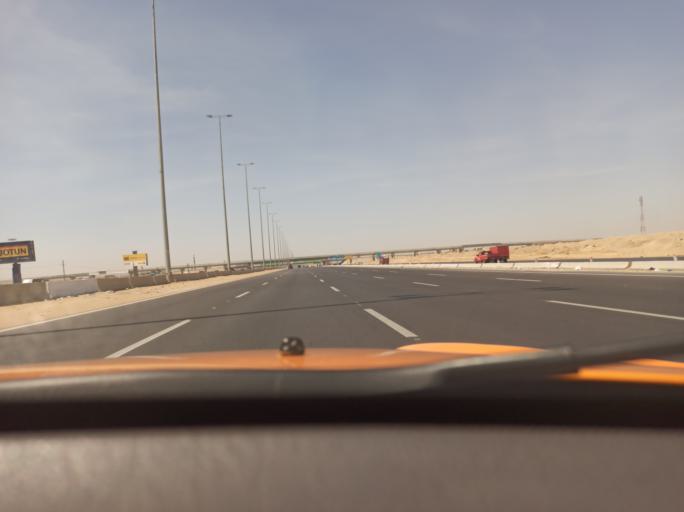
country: EG
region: Eastern Province
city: Bilbays
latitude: 30.2284
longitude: 31.7022
